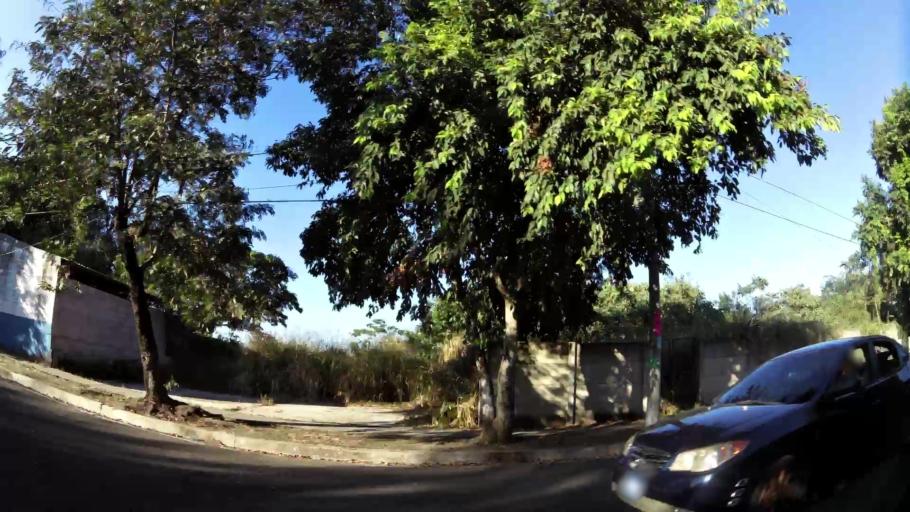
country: SV
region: La Libertad
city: Santa Tecla
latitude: 13.7414
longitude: -89.3588
